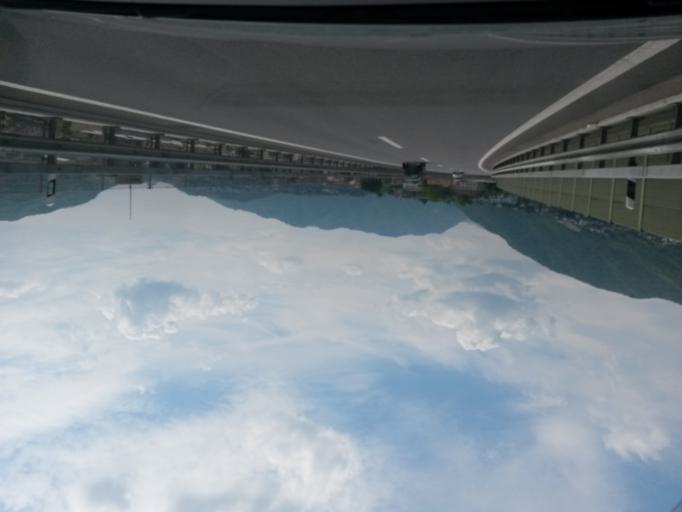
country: CH
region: Ticino
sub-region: Mendrisio District
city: Balerna
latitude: 45.8435
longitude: 9.0032
